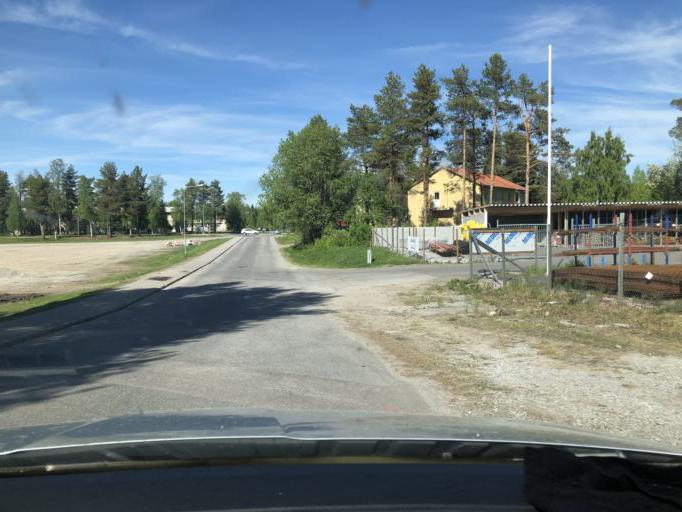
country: SE
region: Norrbotten
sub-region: Jokkmokks Kommun
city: Jokkmokk
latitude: 66.6024
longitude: 19.8465
